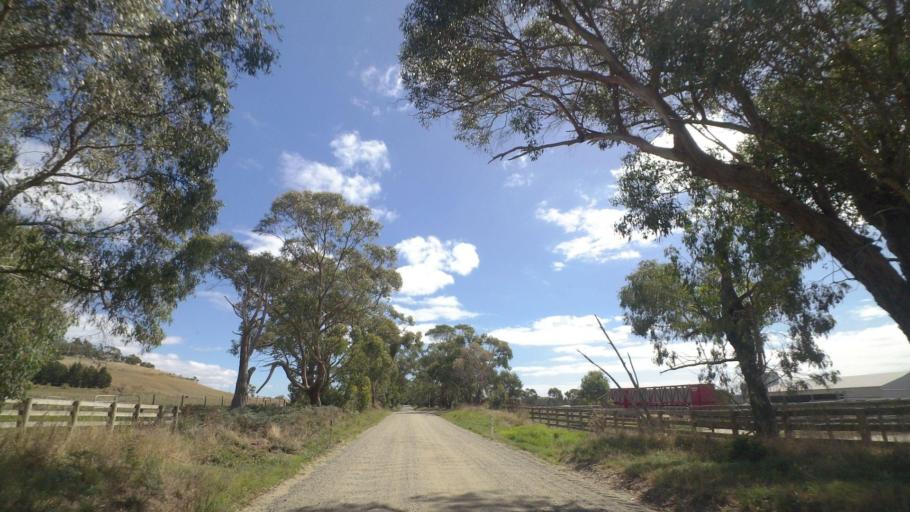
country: AU
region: Victoria
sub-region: Cardinia
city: Bunyip
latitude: -38.3264
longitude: 145.7151
